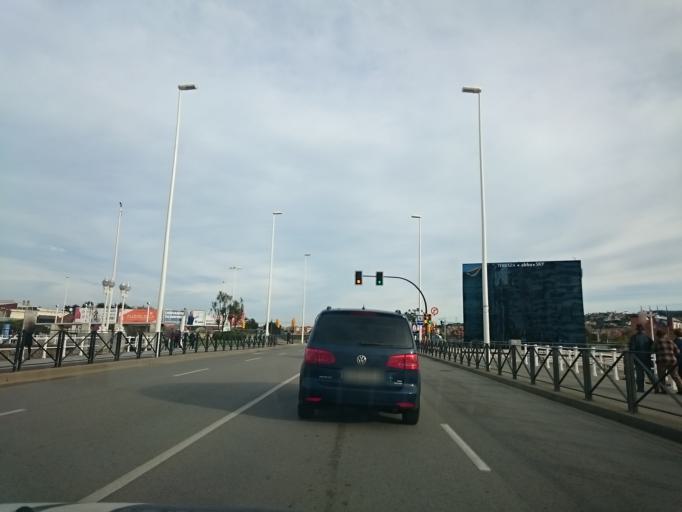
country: ES
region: Asturias
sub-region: Province of Asturias
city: Gijon
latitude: 43.5488
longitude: -5.6157
